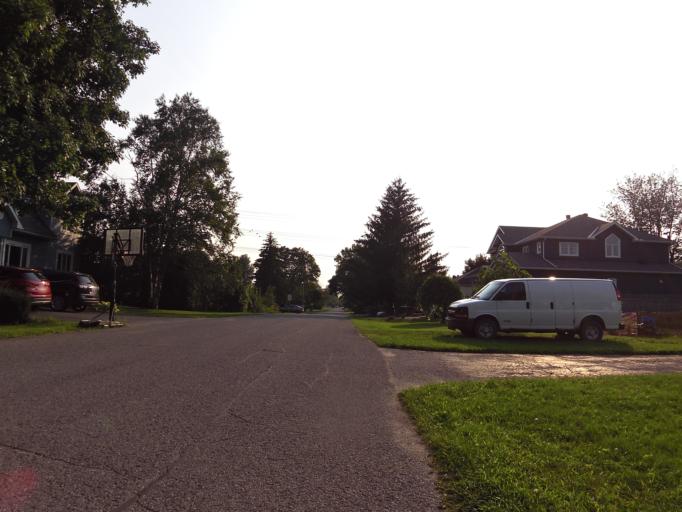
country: CA
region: Ontario
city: Ottawa
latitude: 45.3538
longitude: -75.7419
